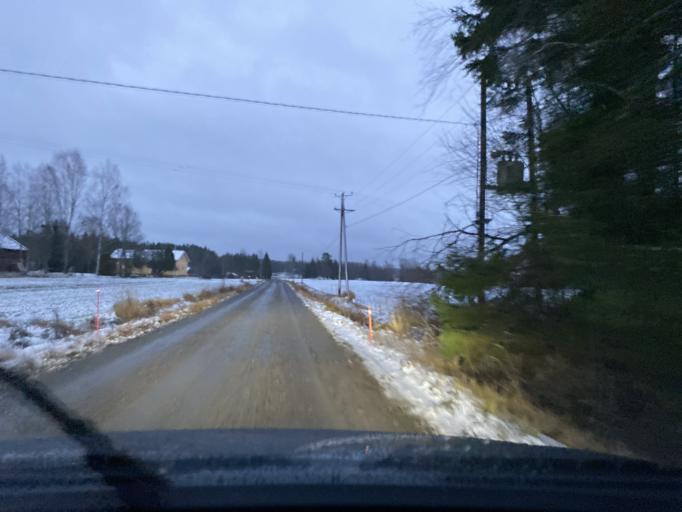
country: FI
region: Pirkanmaa
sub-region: Lounais-Pirkanmaa
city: Punkalaidun
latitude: 61.1627
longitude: 22.9480
